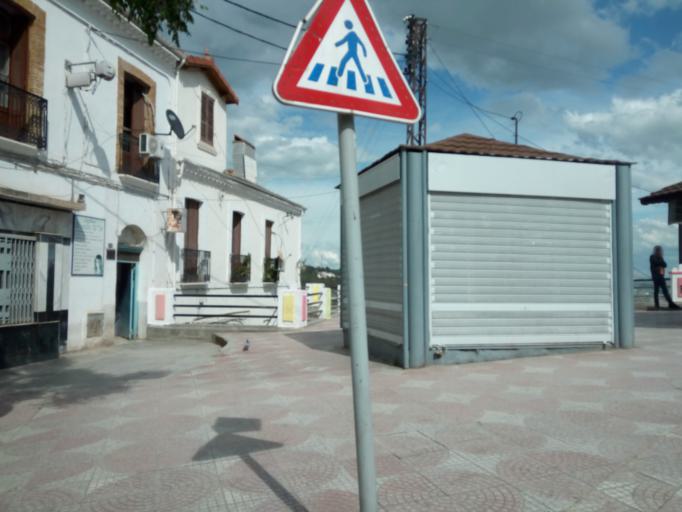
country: DZ
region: Constantine
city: Constantine
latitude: 36.3604
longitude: 6.6068
